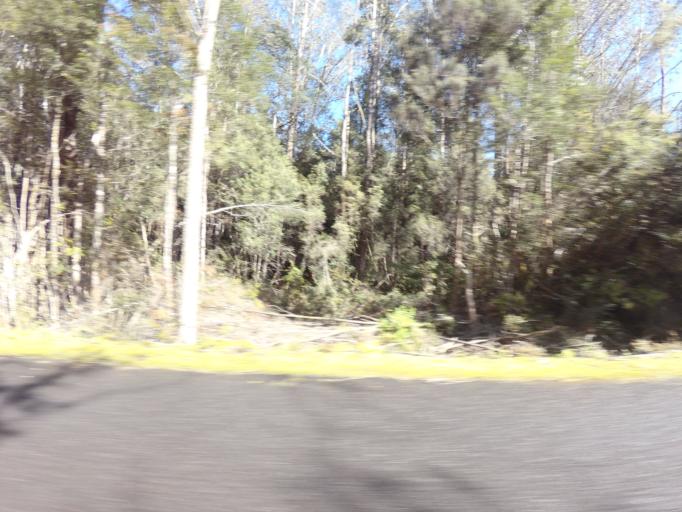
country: AU
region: Tasmania
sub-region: Derwent Valley
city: New Norfolk
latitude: -42.7325
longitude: 146.4261
